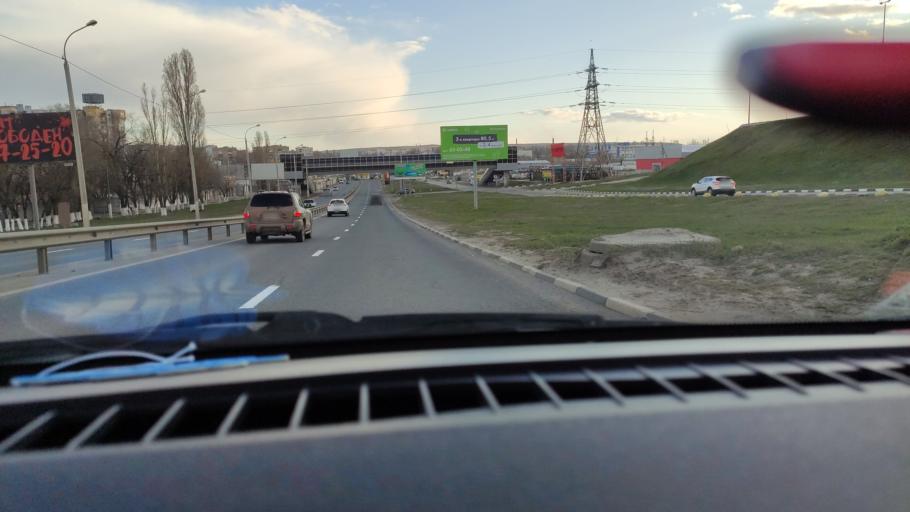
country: RU
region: Saratov
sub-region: Saratovskiy Rayon
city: Saratov
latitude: 51.6171
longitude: 45.9727
